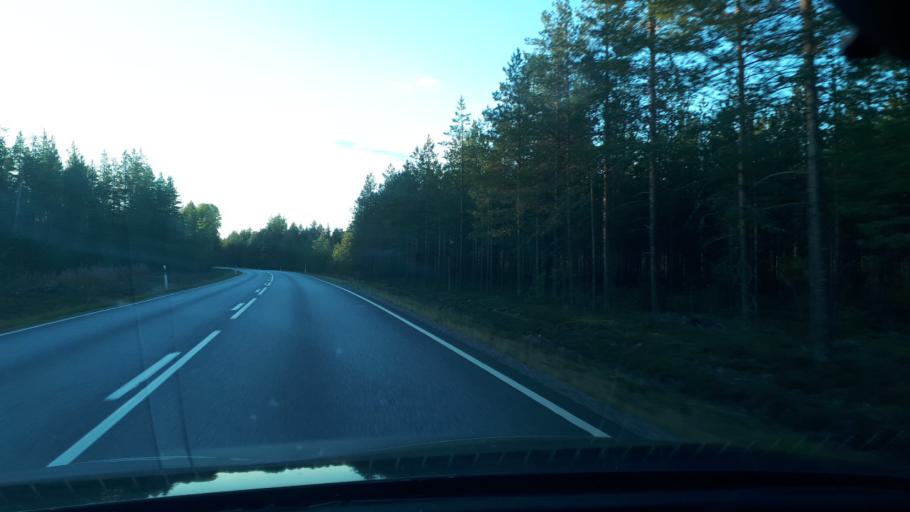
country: FI
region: Northern Ostrobothnia
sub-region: Haapavesi-Siikalatva
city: Pyhaentae
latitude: 64.1267
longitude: 26.2859
